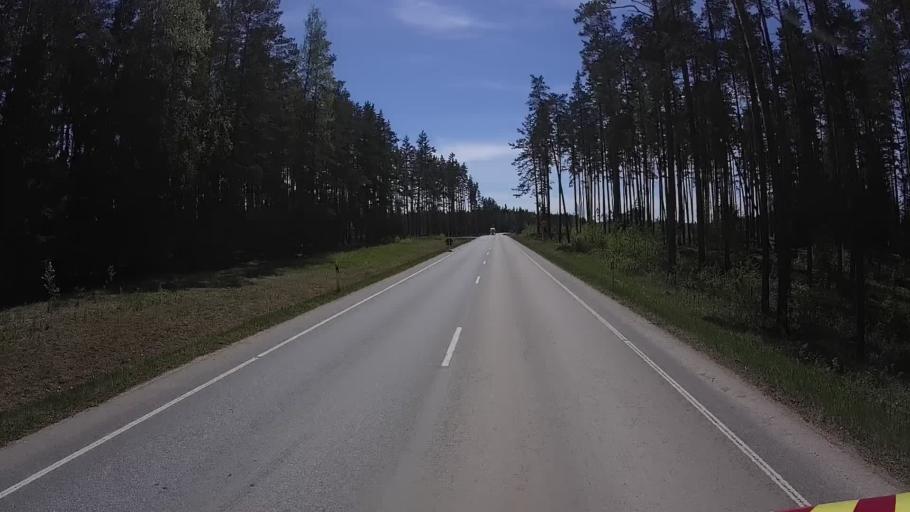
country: EE
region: Polvamaa
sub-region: Polva linn
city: Polva
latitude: 57.9243
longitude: 27.1825
